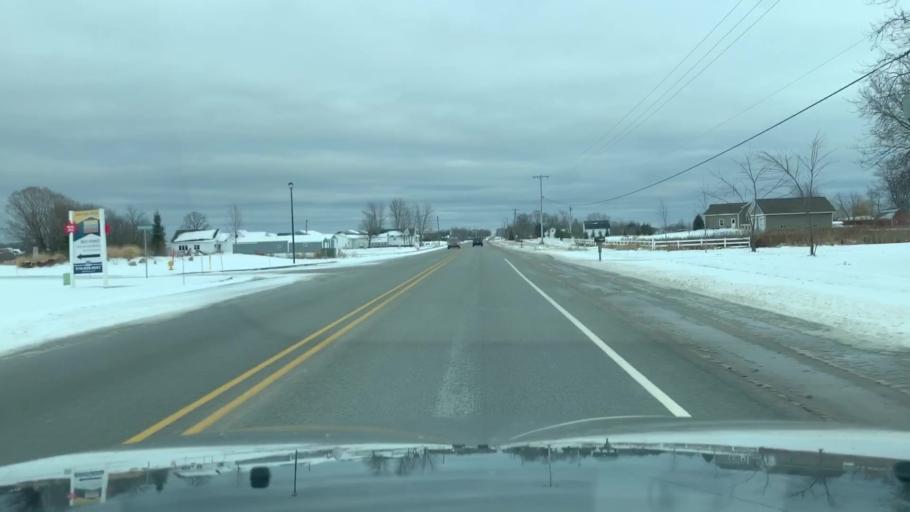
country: US
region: Michigan
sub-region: Ottawa County
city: Zeeland
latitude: 42.8122
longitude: -85.9629
